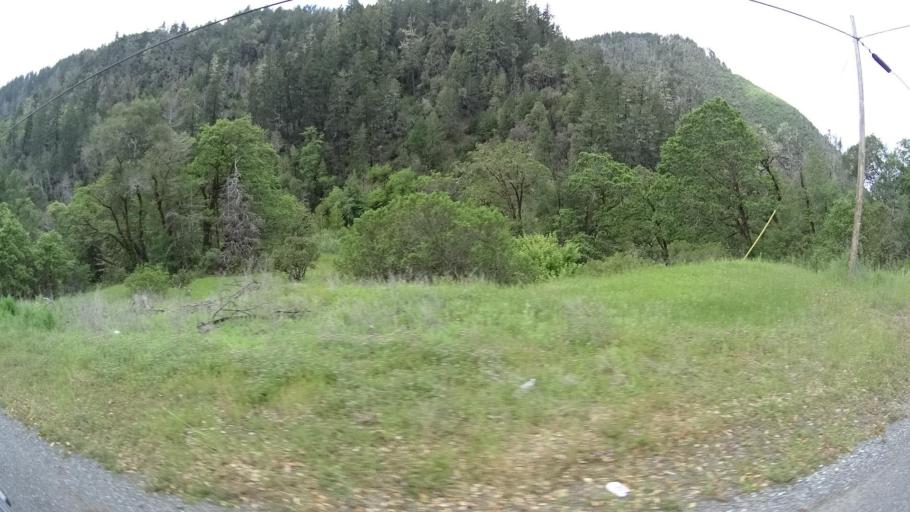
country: US
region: California
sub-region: Humboldt County
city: Redway
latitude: 40.2238
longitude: -123.6049
